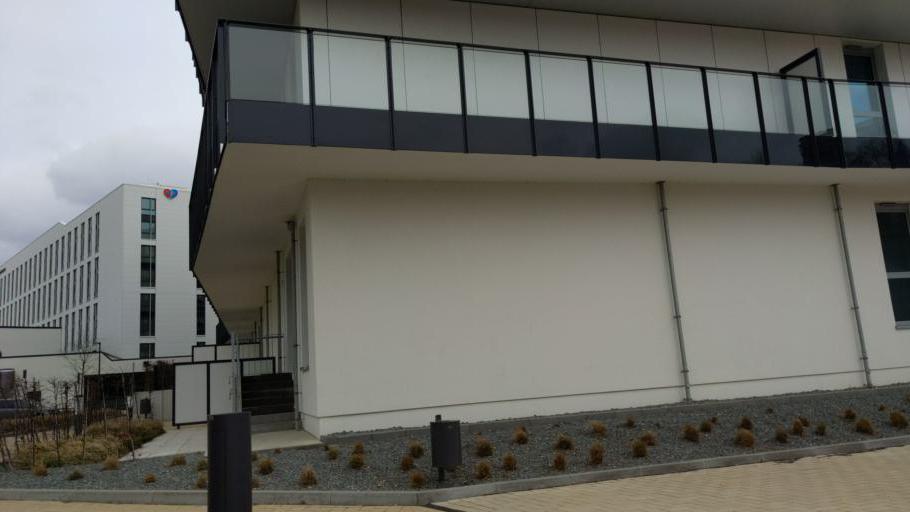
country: DE
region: Schleswig-Holstein
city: Travemuende
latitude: 53.9612
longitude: 10.8805
